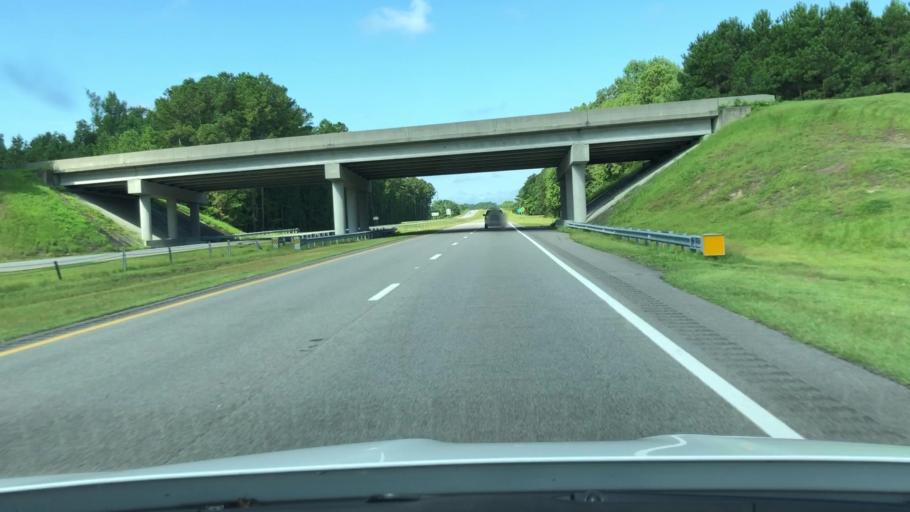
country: US
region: North Carolina
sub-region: Chowan County
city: Edenton
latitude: 36.0920
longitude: -76.5718
